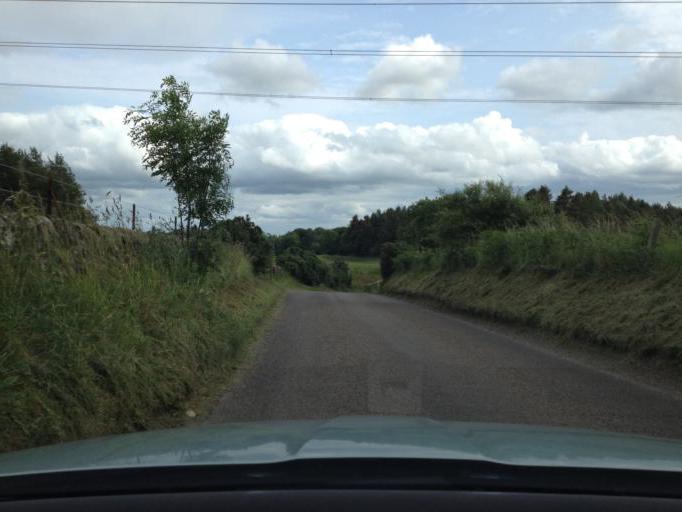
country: GB
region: Scotland
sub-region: Angus
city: Brechin
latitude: 56.8481
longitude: -2.6761
